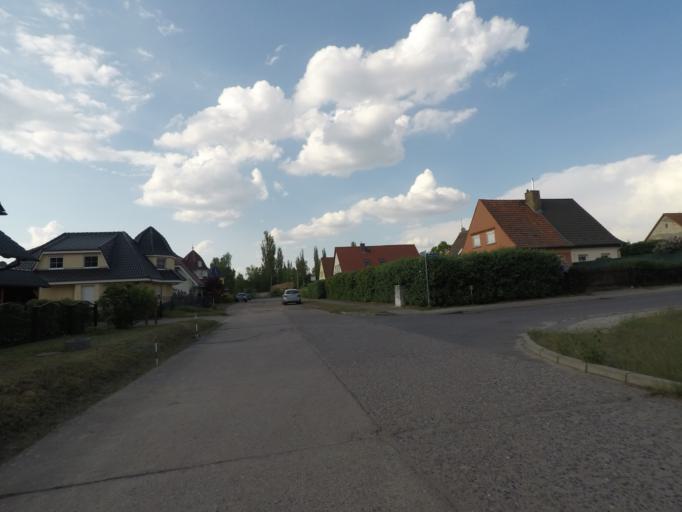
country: DE
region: Brandenburg
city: Melchow
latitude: 52.8319
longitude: 13.7317
